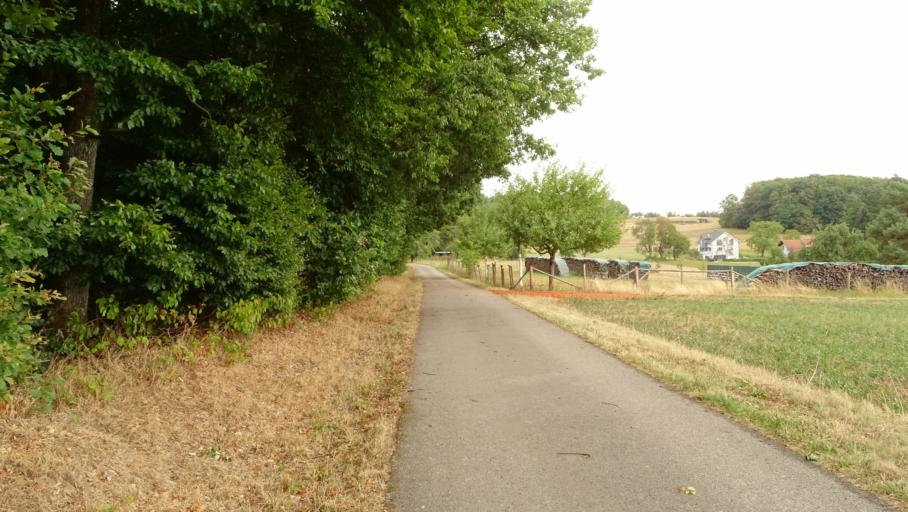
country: DE
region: Baden-Wuerttemberg
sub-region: Karlsruhe Region
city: Fahrenbach
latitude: 49.4301
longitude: 9.1376
